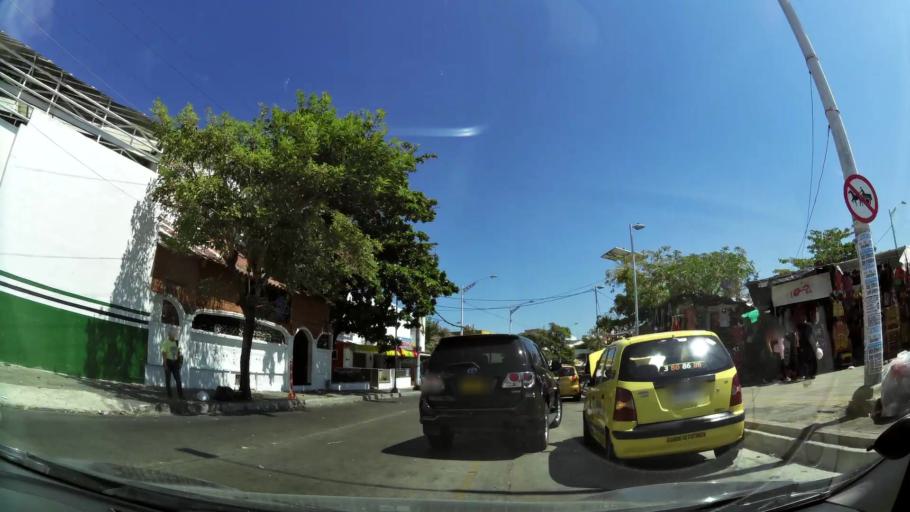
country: CO
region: Atlantico
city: Barranquilla
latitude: 10.9955
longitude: -74.8074
